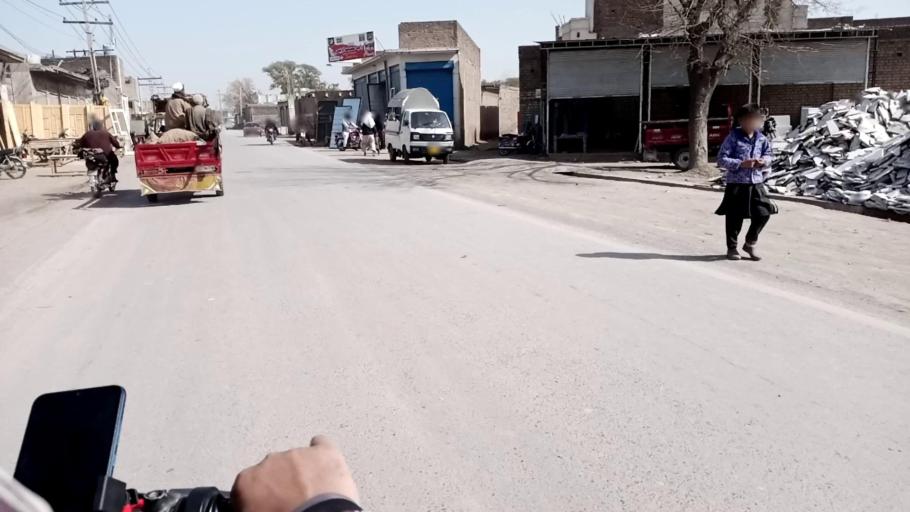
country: PK
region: Khyber Pakhtunkhwa
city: Peshawar
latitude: 34.0023
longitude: 71.6380
